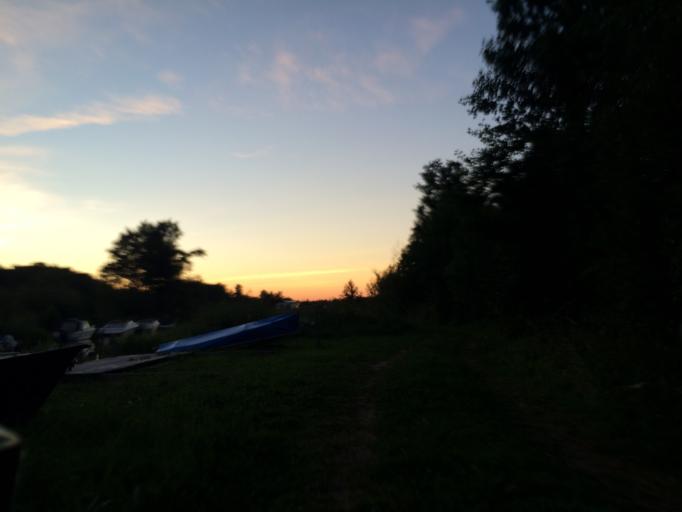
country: SE
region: Soedermanland
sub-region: Eskilstuna Kommun
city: Kvicksund
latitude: 59.4488
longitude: 16.3157
